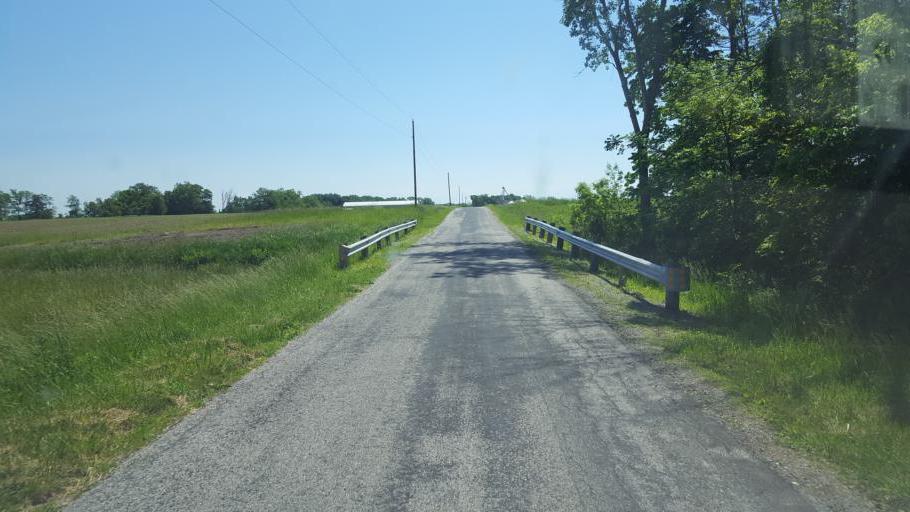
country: US
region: Ohio
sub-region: Hardin County
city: Forest
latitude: 40.6508
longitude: -83.4154
